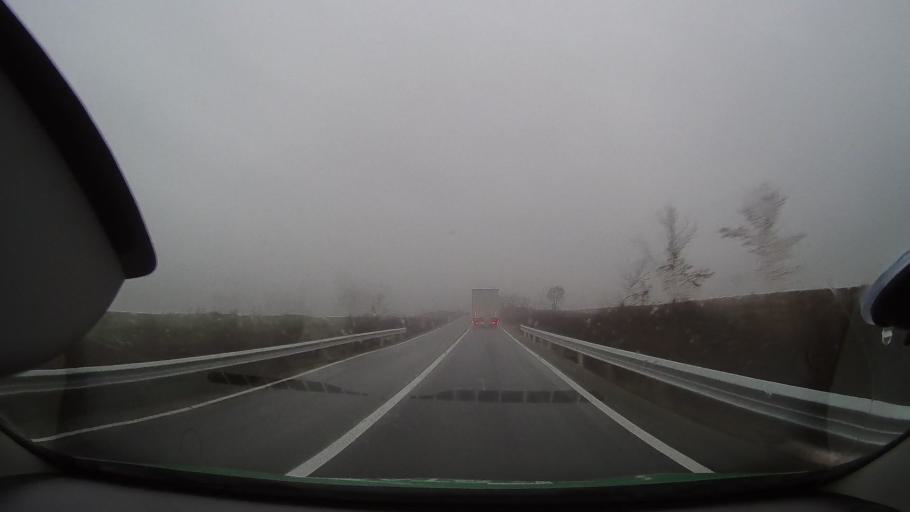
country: RO
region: Bihor
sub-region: Comuna Olcea
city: Olcea
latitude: 46.6717
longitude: 21.9645
